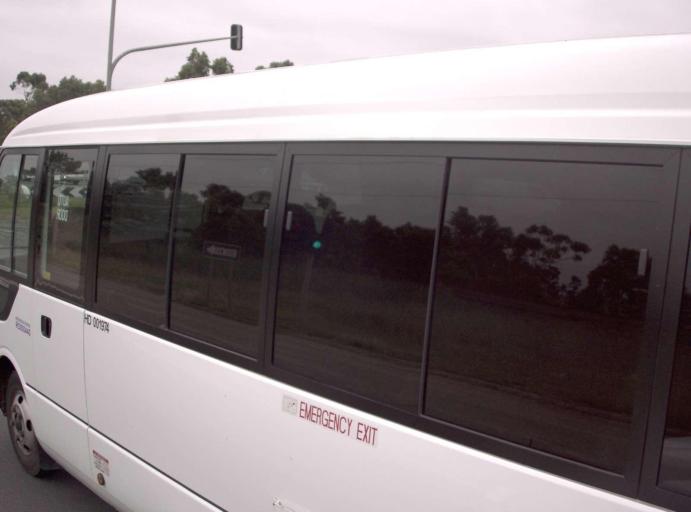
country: AU
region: Victoria
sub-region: Latrobe
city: Traralgon
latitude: -38.2208
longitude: 146.4718
